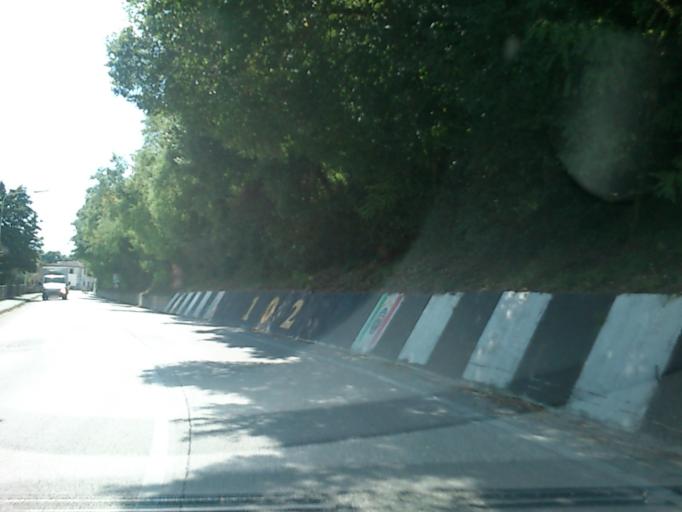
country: IT
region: The Marches
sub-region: Provincia di Pesaro e Urbino
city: Tavernelle
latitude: 43.7351
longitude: 12.8861
